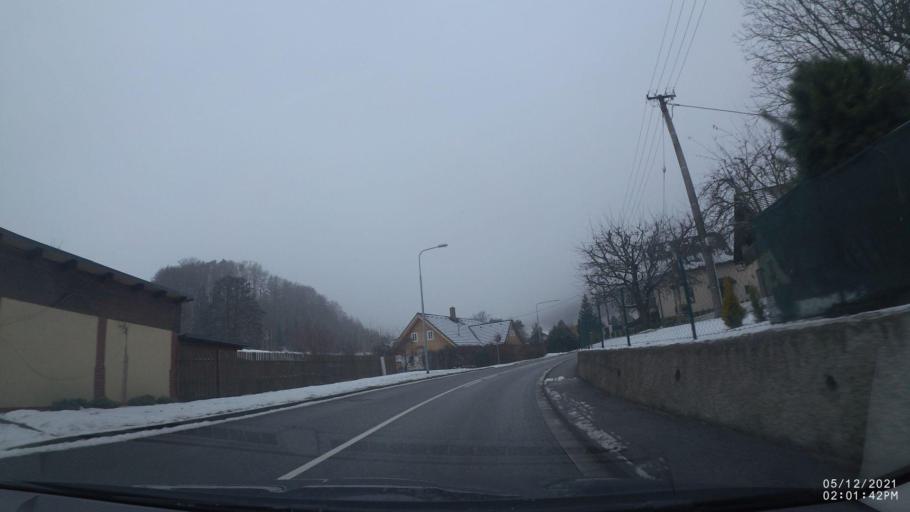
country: CZ
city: Hronov
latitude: 50.4827
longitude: 16.1521
